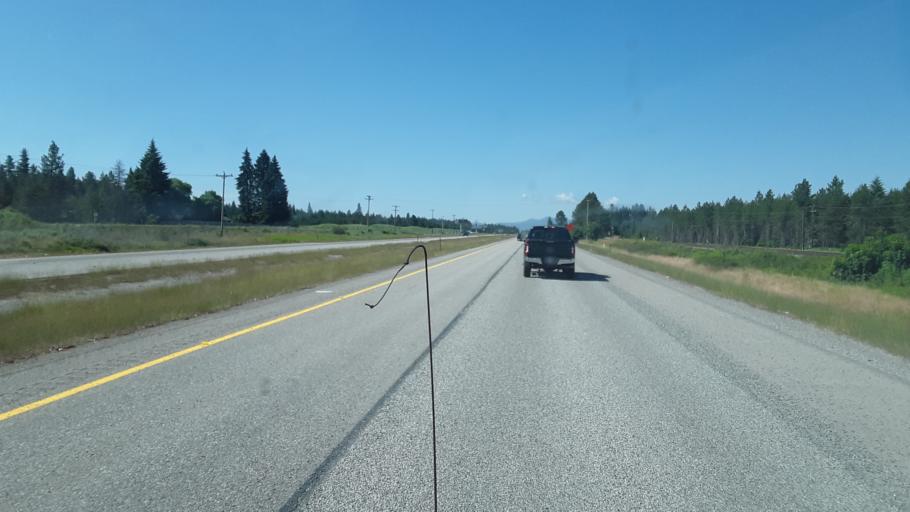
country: US
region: Idaho
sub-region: Kootenai County
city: Hayden
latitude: 47.8454
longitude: -116.7650
